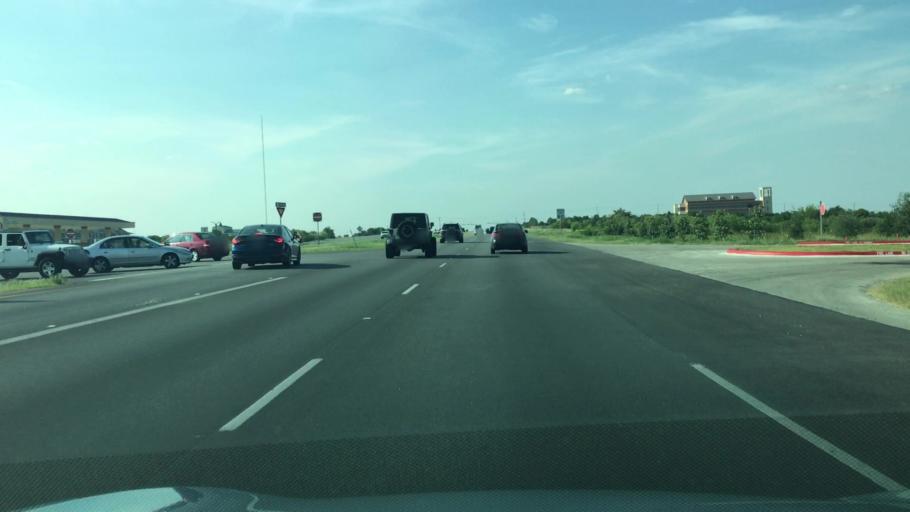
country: US
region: Texas
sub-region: Hays County
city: Kyle
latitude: 30.0208
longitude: -97.8720
